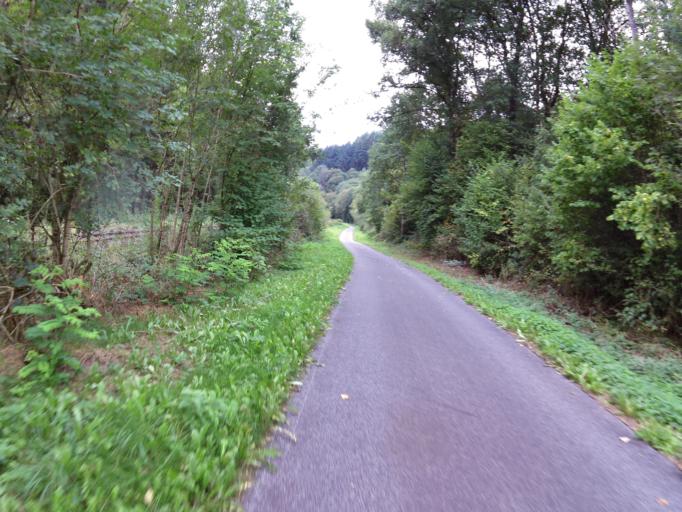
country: DE
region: Rheinland-Pfalz
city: Zendscheid
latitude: 50.0834
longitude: 6.6036
